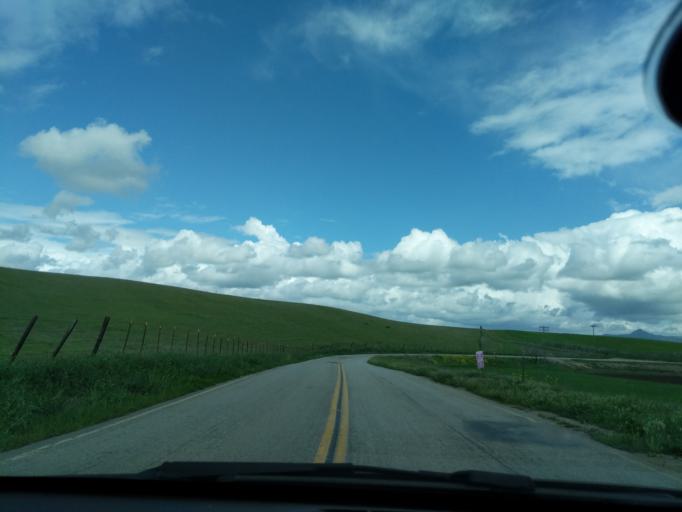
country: US
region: California
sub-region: San Benito County
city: Hollister
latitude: 36.8694
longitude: -121.4356
